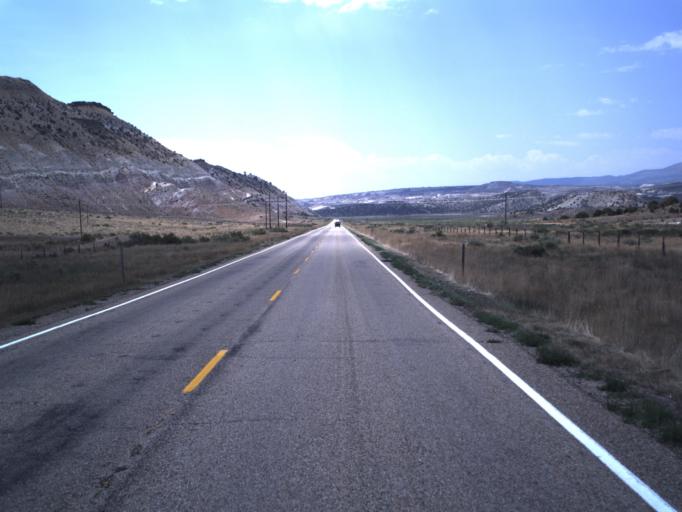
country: US
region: Utah
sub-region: Uintah County
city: Vernal
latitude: 40.5622
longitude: -109.5058
